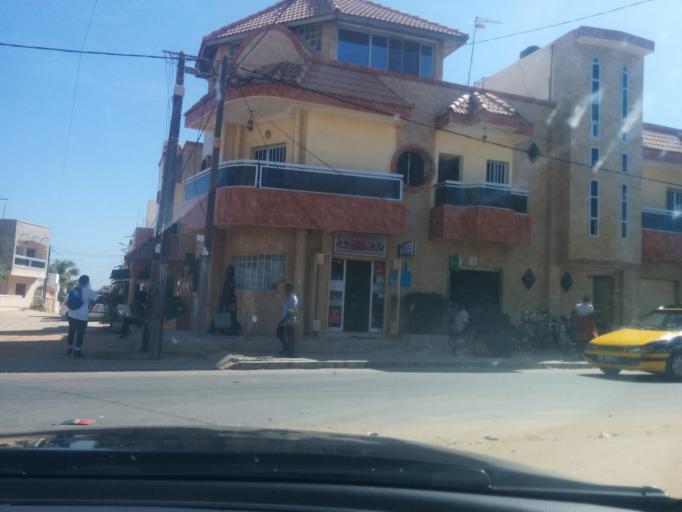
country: SN
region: Dakar
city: Grand Dakar
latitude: 14.7477
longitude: -17.4419
